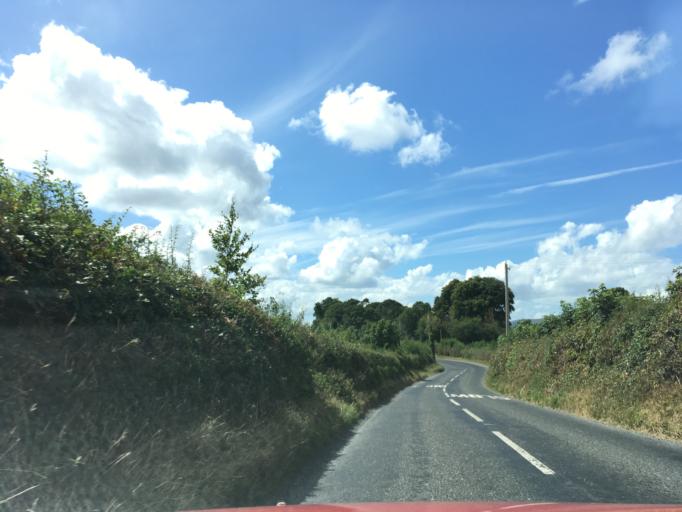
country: IE
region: Munster
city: Cahir
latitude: 52.3484
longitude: -7.9361
